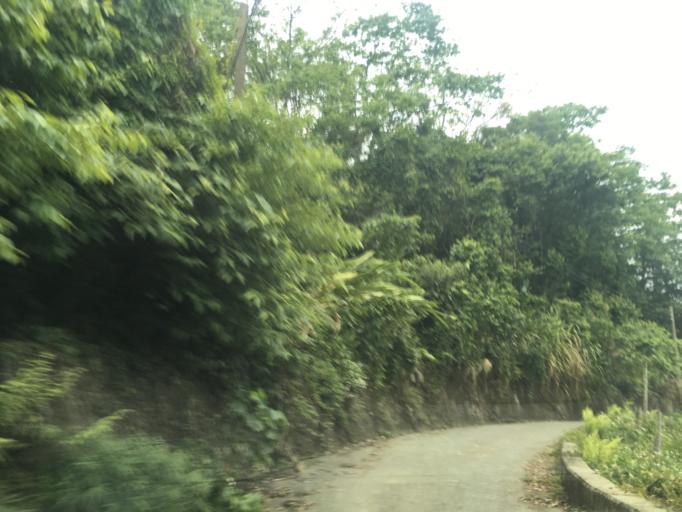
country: TW
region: Taiwan
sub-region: Taichung City
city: Taichung
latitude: 24.1458
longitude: 120.8221
